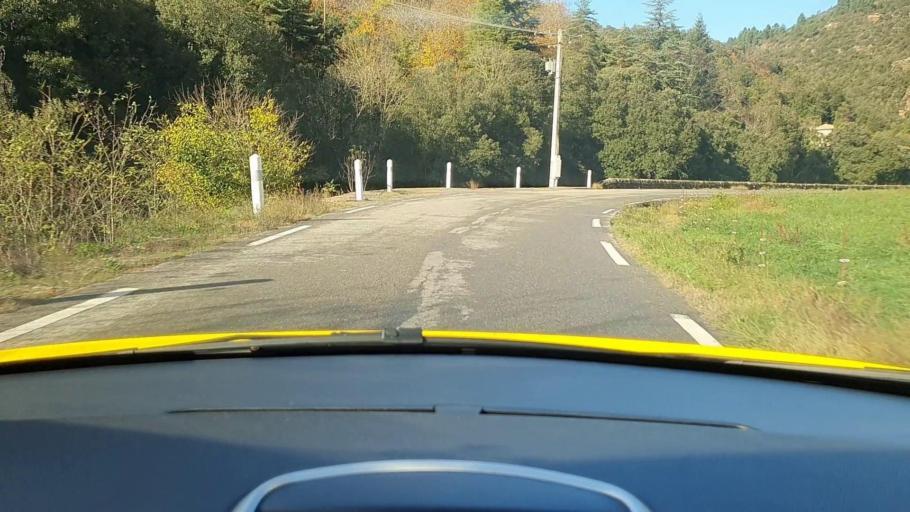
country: FR
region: Languedoc-Roussillon
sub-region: Departement du Gard
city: Valleraugue
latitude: 44.1384
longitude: 3.7338
